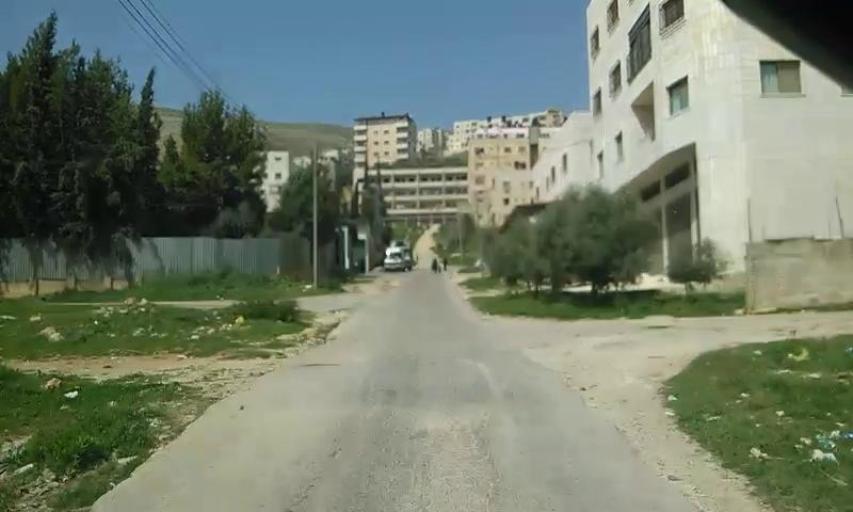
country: PS
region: West Bank
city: `Azmut
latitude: 32.2224
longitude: 35.2973
